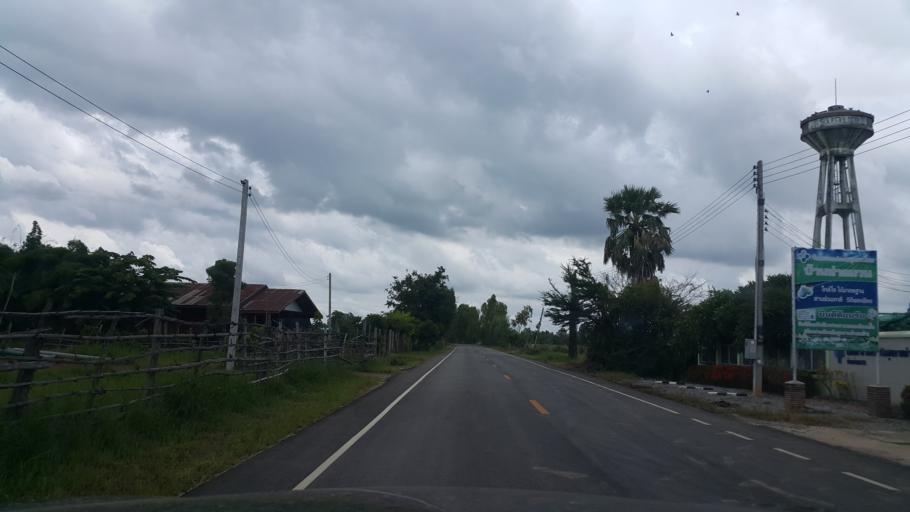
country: TH
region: Sukhothai
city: Kong Krailat
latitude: 16.9200
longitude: 99.8877
